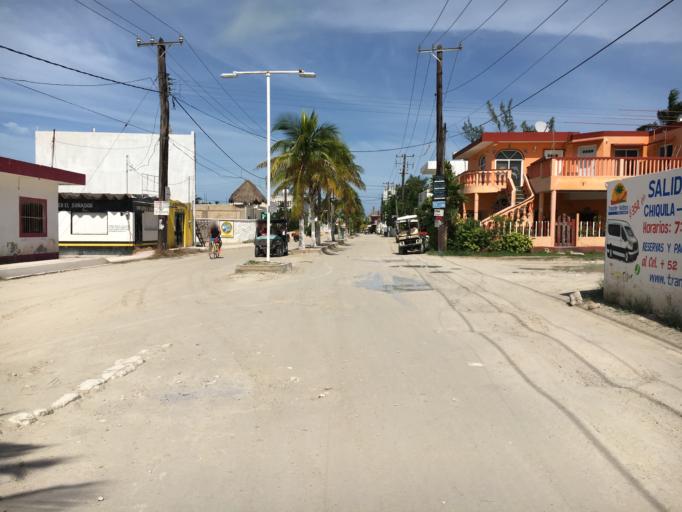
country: MX
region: Quintana Roo
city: Kantunilkin
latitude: 21.5205
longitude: -87.3763
